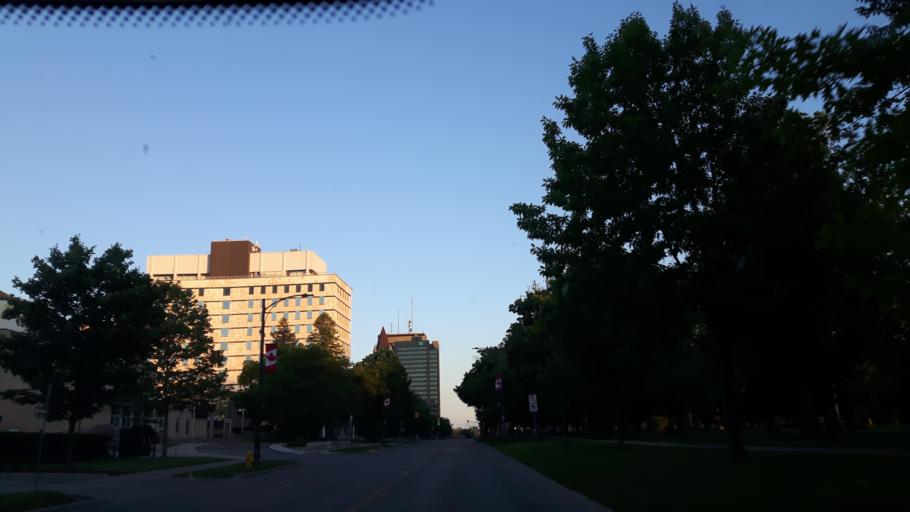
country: CA
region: Ontario
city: London
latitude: 42.9896
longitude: -81.2477
